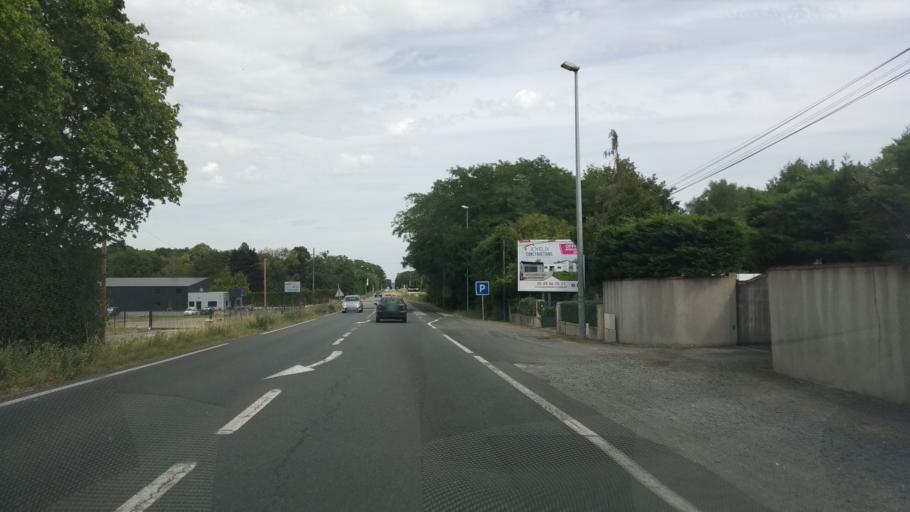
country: FR
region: Poitou-Charentes
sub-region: Departement de la Vienne
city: Mignaloux-Beauvoir
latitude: 46.5633
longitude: 0.4099
